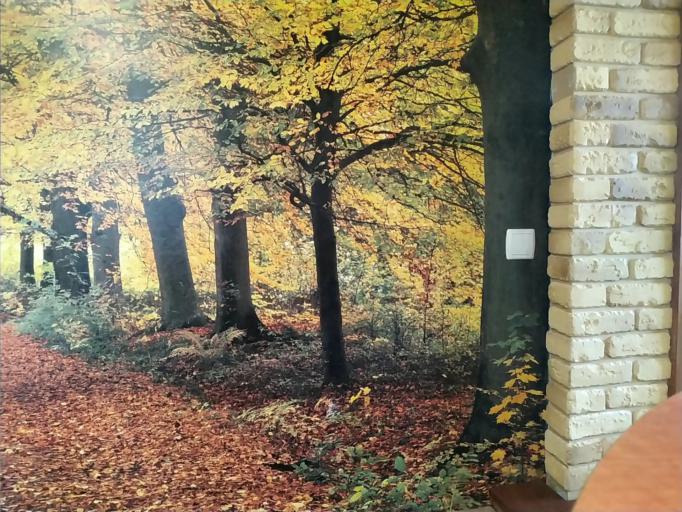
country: RU
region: Arkhangelskaya
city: Kargopol'
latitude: 60.9101
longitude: 38.8826
